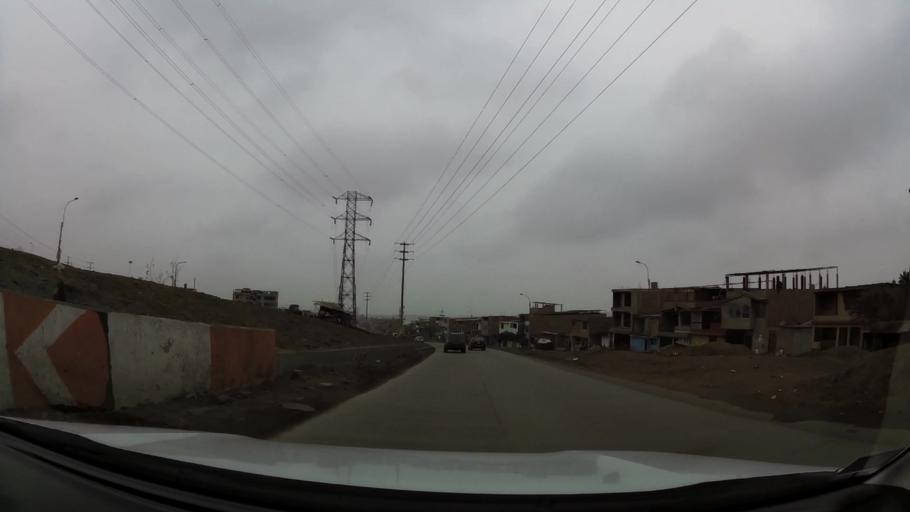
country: PE
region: Lima
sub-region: Lima
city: Surco
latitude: -12.2158
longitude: -76.9221
